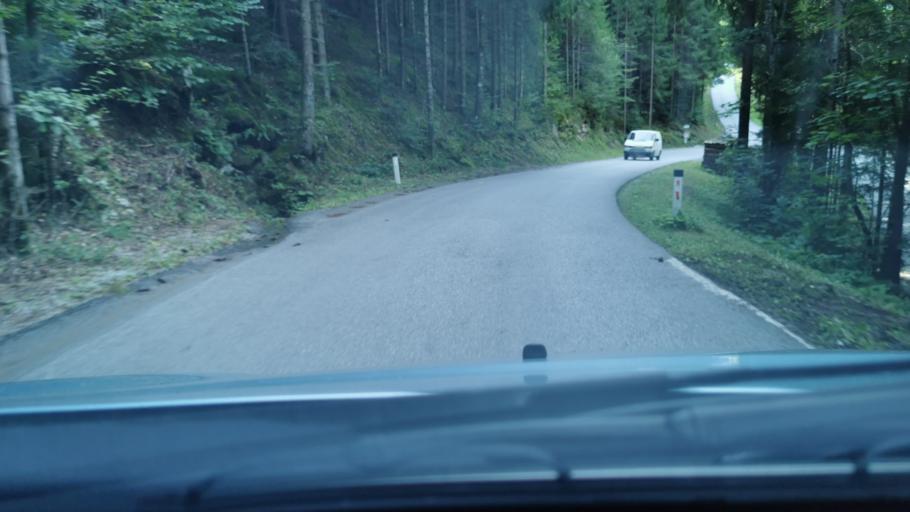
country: AT
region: Styria
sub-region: Politischer Bezirk Weiz
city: Koglhof
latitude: 47.3322
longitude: 15.7005
